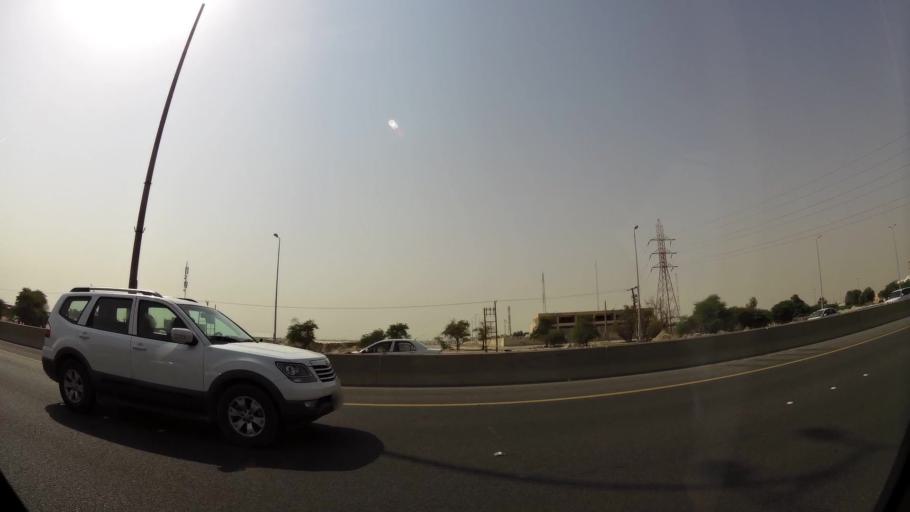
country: KW
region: Muhafazat al Jahra'
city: Al Jahra'
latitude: 29.3377
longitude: 47.7202
